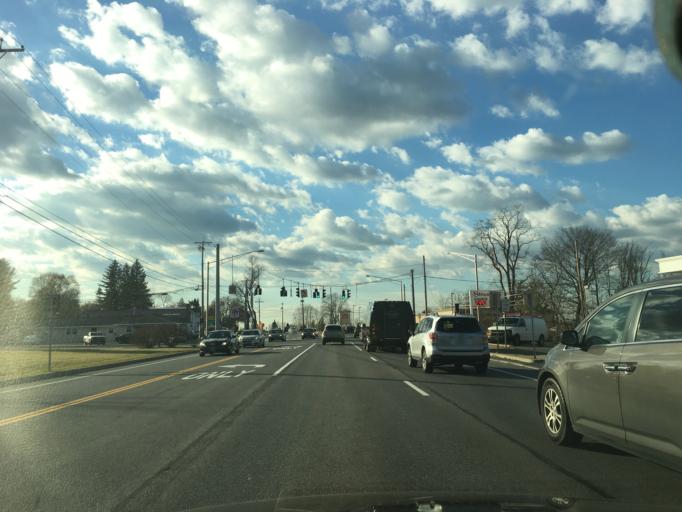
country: US
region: New York
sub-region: Rensselaer County
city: Hampton Manor
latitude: 42.6510
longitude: -73.6961
